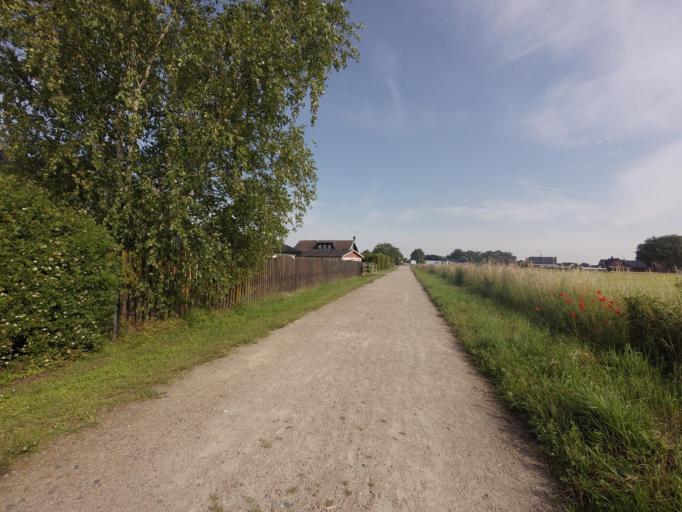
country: SE
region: Skane
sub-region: Vellinge Kommun
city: Vellinge
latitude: 55.4900
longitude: 13.0135
